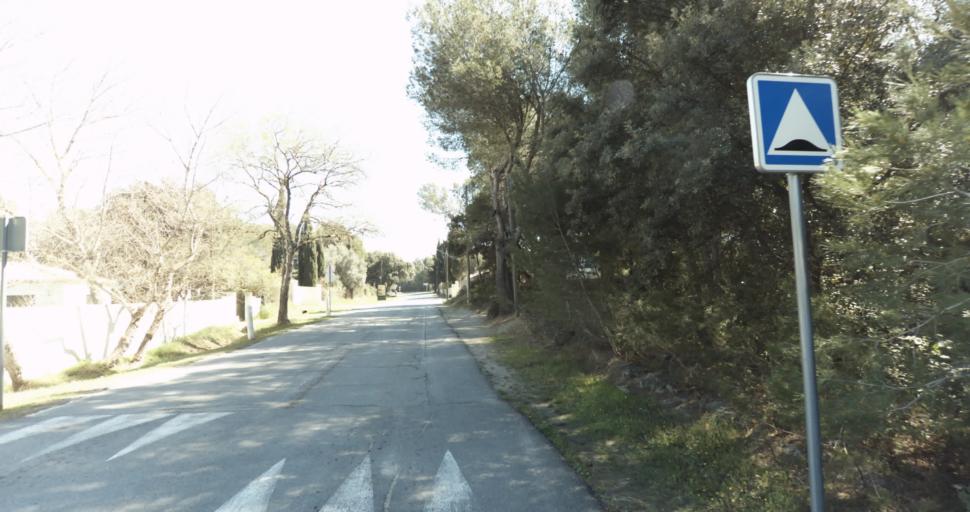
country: FR
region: Provence-Alpes-Cote d'Azur
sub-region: Departement des Bouches-du-Rhone
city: Pelissanne
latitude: 43.6347
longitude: 5.1648
